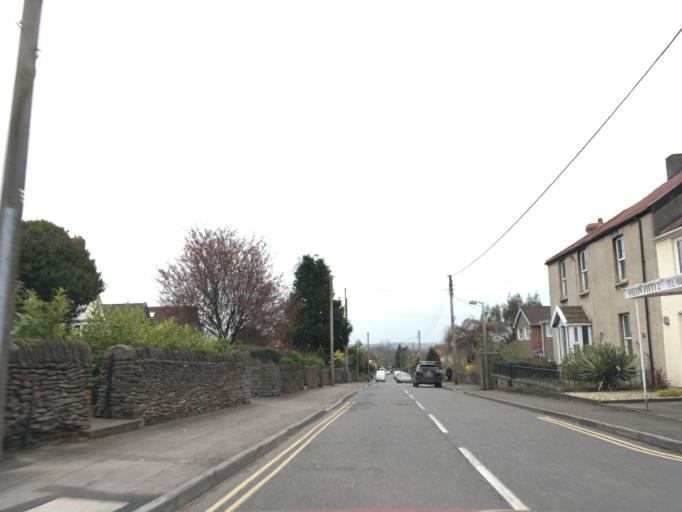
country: GB
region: England
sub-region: South Gloucestershire
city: Winterbourne
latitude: 51.5148
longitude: -2.5028
